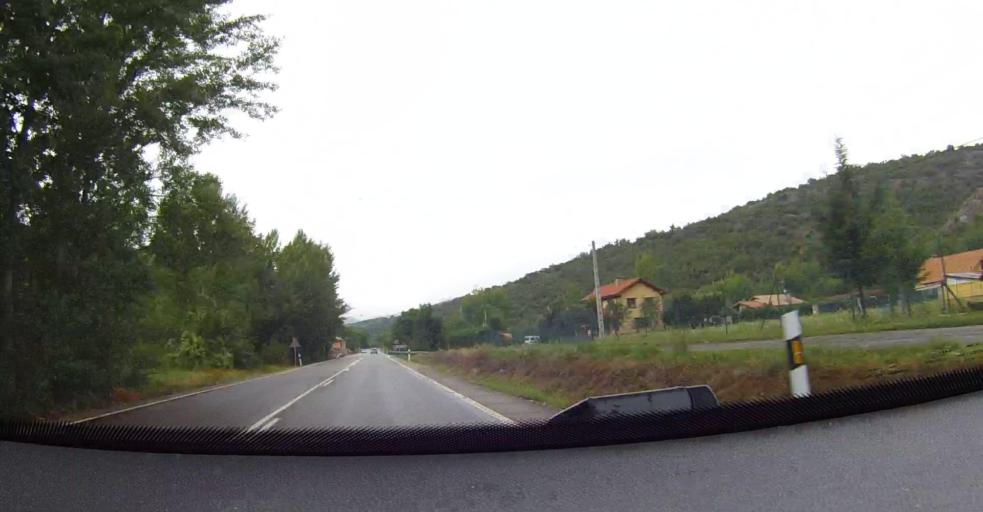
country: ES
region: Castille and Leon
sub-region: Provincia de Leon
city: Cistierna
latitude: 42.8261
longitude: -5.1210
